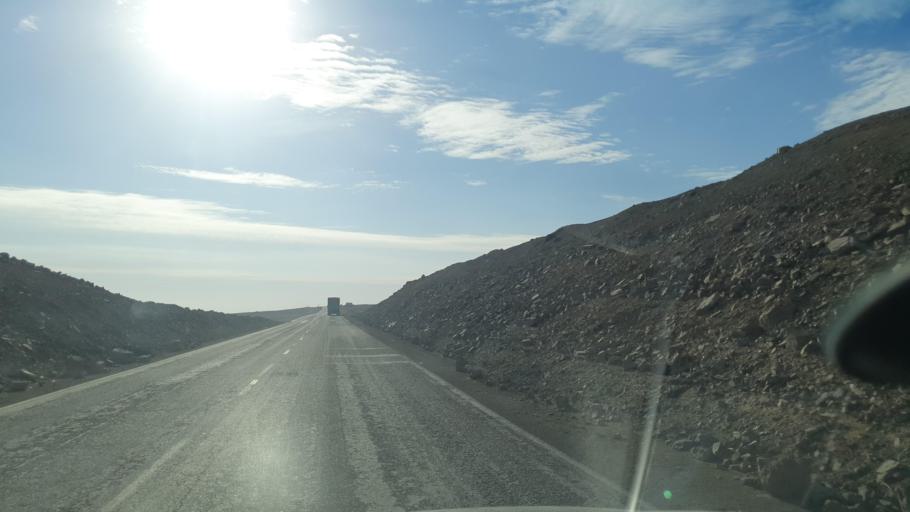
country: KZ
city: Priozersk
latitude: 45.8240
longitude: 73.4481
